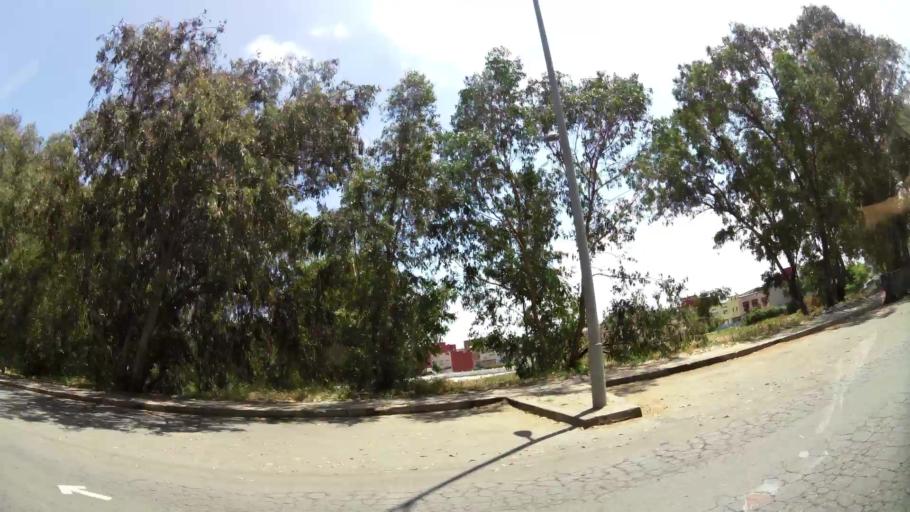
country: MA
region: Gharb-Chrarda-Beni Hssen
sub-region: Kenitra Province
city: Kenitra
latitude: 34.2620
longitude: -6.6126
